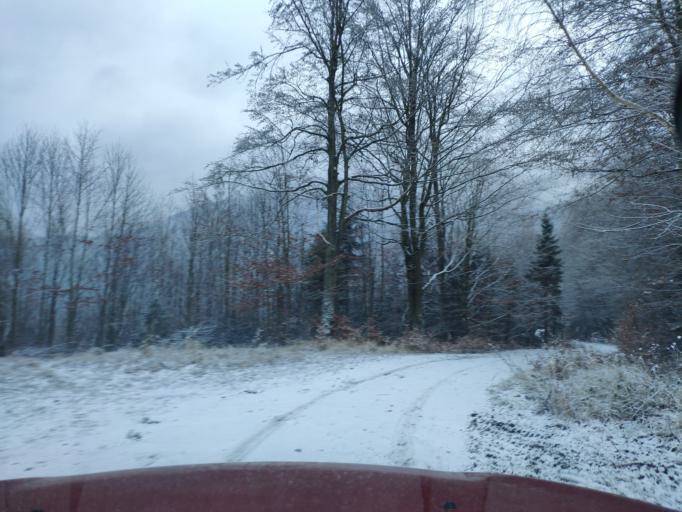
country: SK
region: Kosicky
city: Spisska Nova Ves
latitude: 48.8150
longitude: 20.5133
